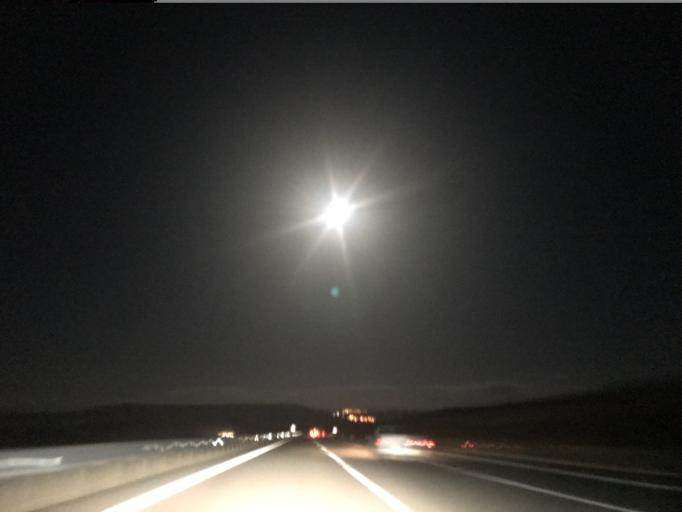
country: TR
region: Nigde
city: Ulukisla
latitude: 37.6352
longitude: 34.4261
